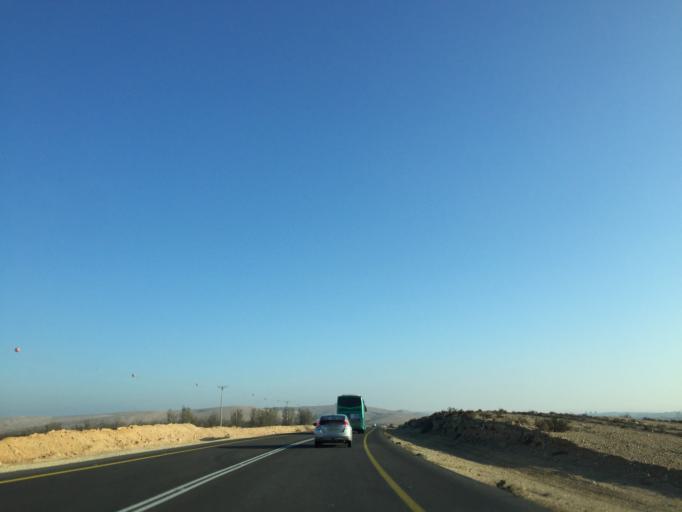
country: IL
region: Southern District
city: Dimona
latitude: 31.0414
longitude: 34.9782
